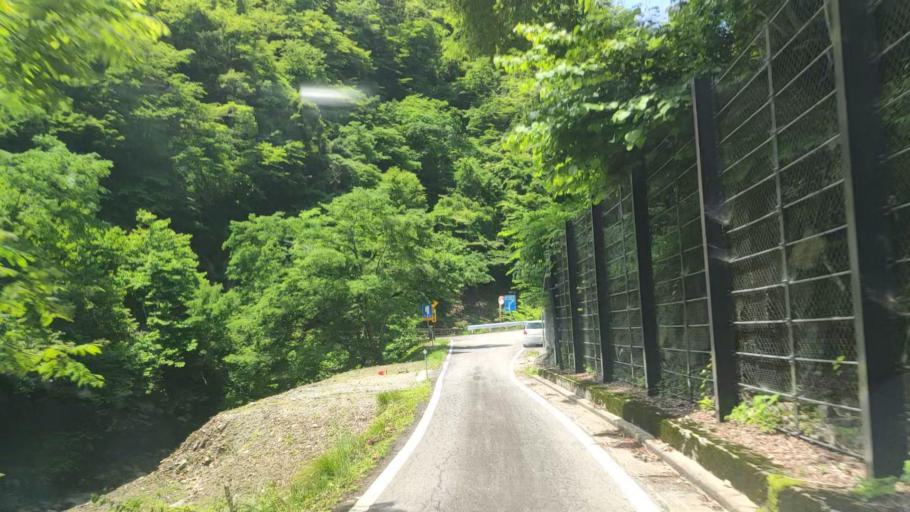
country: JP
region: Tottori
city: Tottori
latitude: 35.4019
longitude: 134.5014
